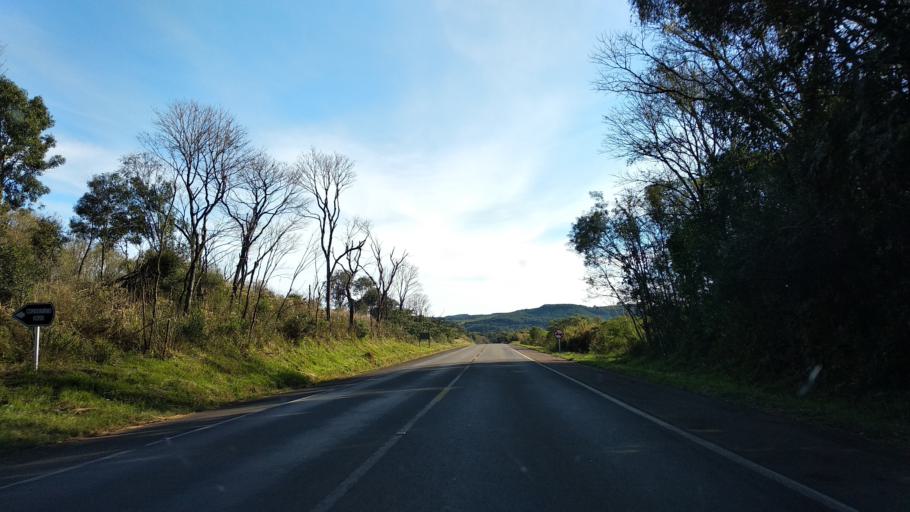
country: BR
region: Santa Catarina
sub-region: Celso Ramos
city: Celso Ramos
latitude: -27.5458
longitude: -51.4286
